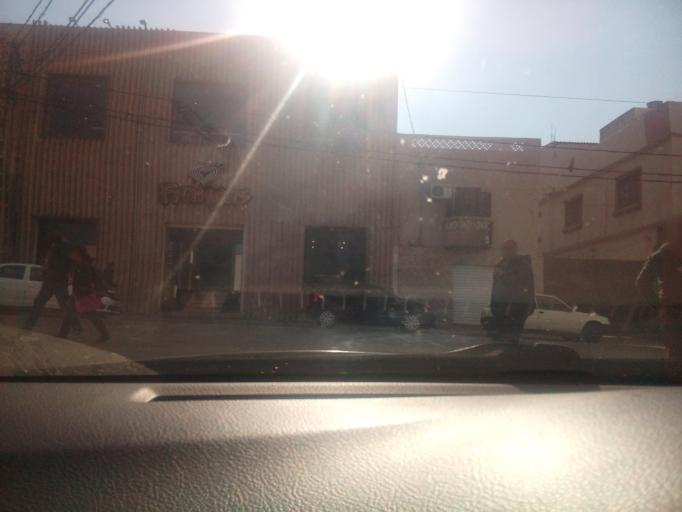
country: DZ
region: Oran
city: Oran
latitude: 35.7074
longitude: -0.6235
